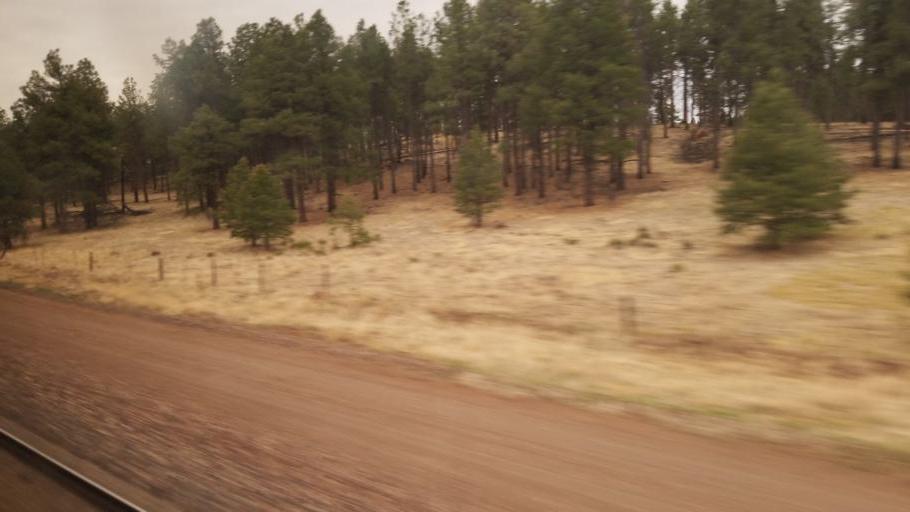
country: US
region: Arizona
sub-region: Coconino County
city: Parks
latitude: 35.2458
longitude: -112.0392
